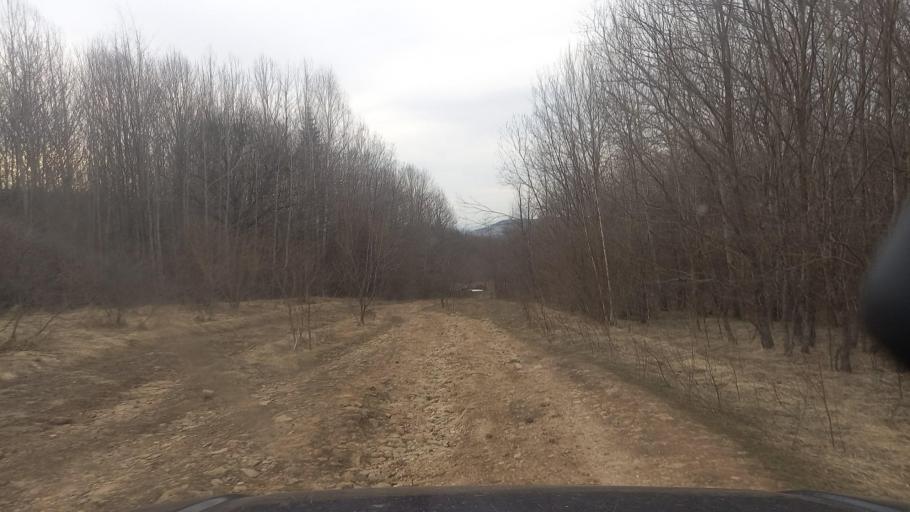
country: RU
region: Adygeya
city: Kamennomostskiy
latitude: 44.1664
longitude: 40.0116
